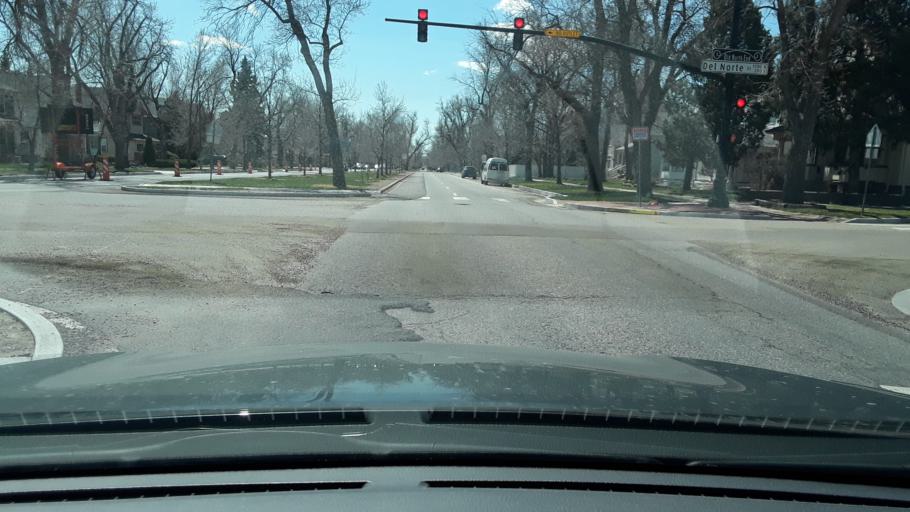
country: US
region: Colorado
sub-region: El Paso County
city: Colorado Springs
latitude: 38.8579
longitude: -104.8205
